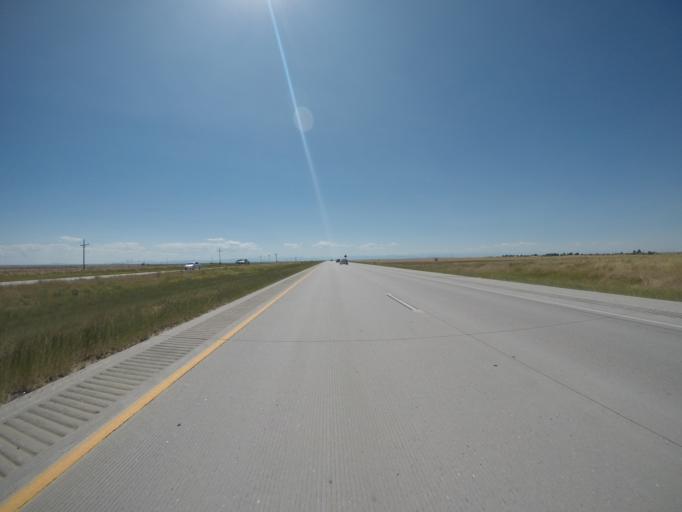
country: US
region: Colorado
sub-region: Adams County
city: Bennett
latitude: 39.7396
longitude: -104.5597
